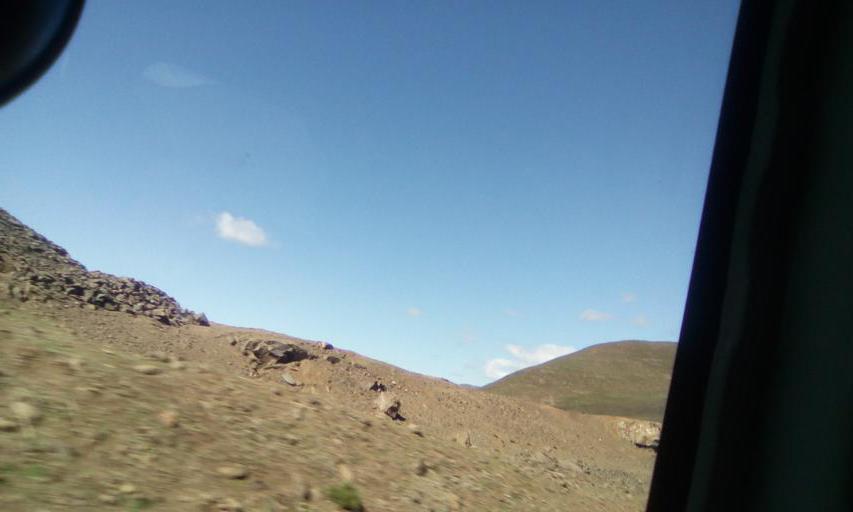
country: LS
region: Maseru
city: Nako
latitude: -29.8860
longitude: 28.0922
